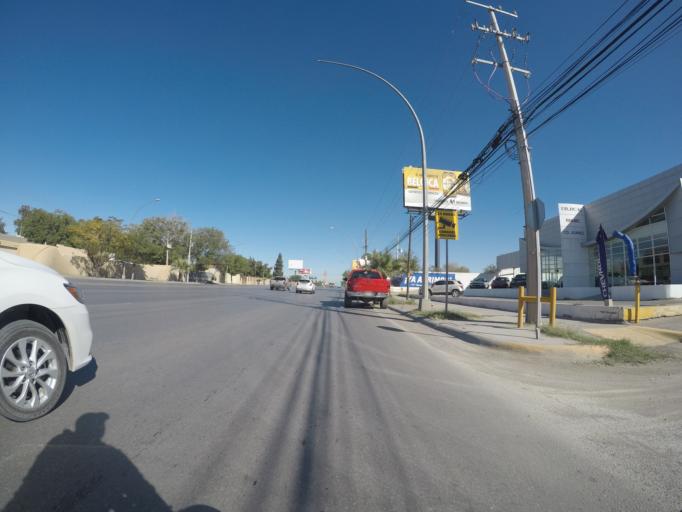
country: MX
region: Chihuahua
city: Ciudad Juarez
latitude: 31.7280
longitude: -106.4251
